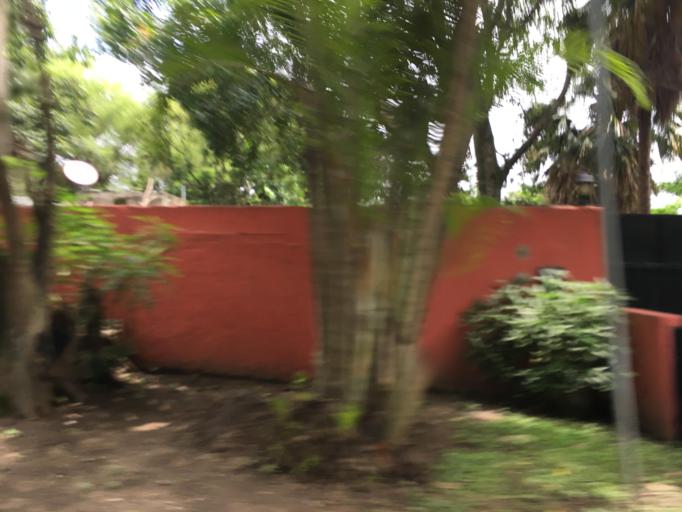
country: GT
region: Guatemala
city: Villa Canales
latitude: 14.4195
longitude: -90.5402
